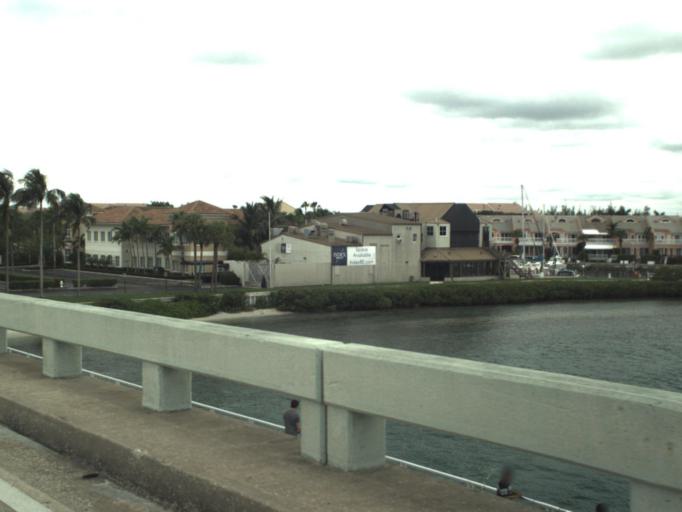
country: US
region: Florida
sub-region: Palm Beach County
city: Jupiter
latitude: 26.9469
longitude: -80.0849
